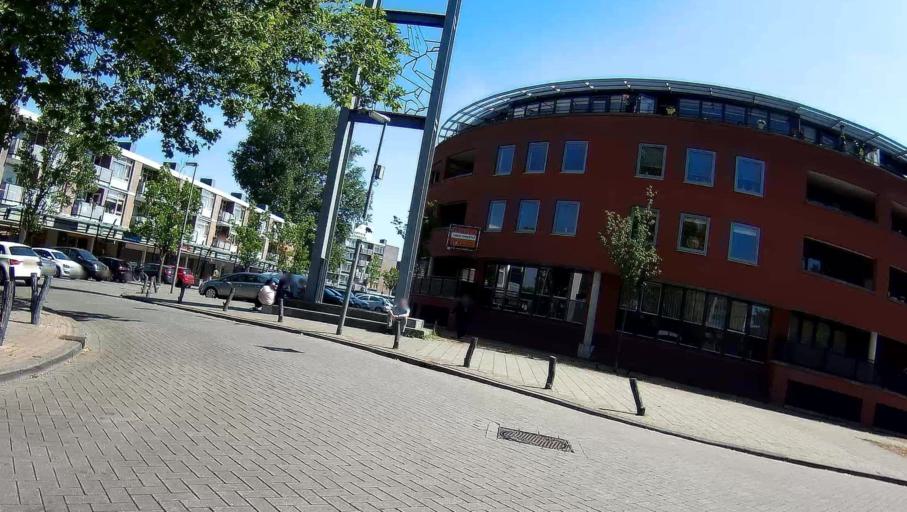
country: NL
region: South Holland
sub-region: Gemeente Schiedam
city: Schiedam
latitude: 51.9219
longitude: 4.3915
